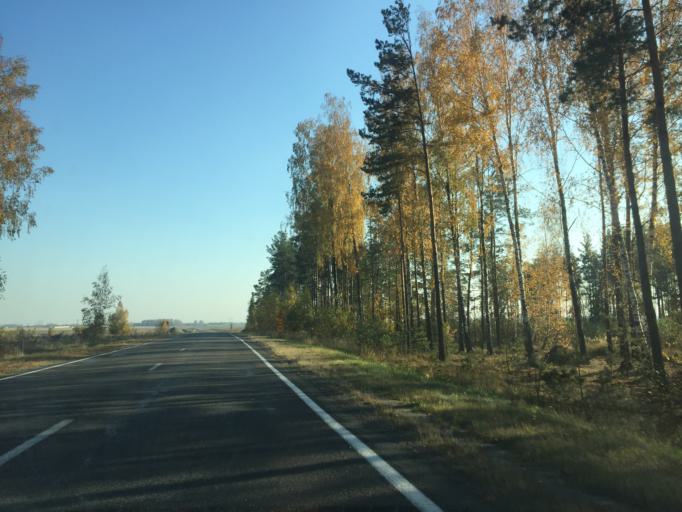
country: BY
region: Gomel
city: Dobrush
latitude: 52.3297
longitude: 31.2400
